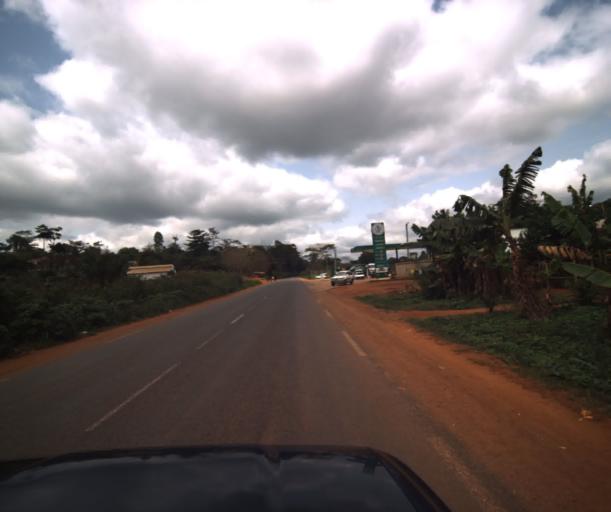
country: CM
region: Centre
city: Mbankomo
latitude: 3.7884
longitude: 11.4316
